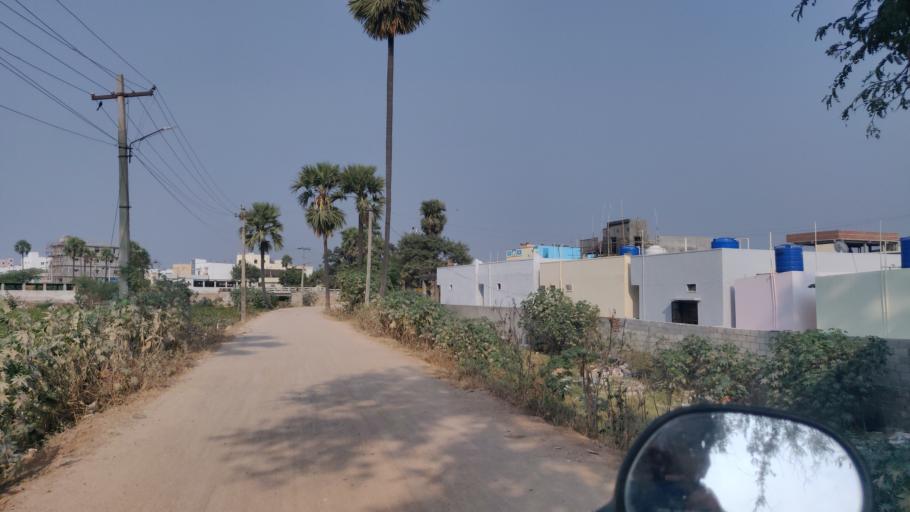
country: IN
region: Telangana
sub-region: Rangareddi
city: Uppal Kalan
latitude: 17.3931
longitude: 78.6043
